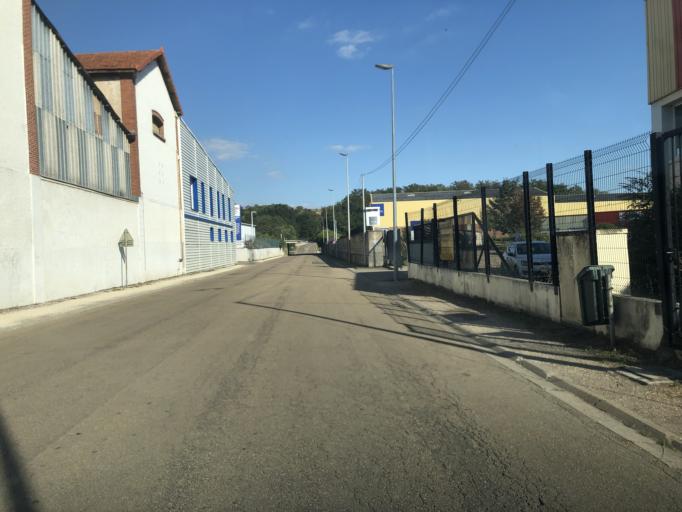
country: FR
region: Bourgogne
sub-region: Departement de l'Yonne
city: Auxerre
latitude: 47.8064
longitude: 3.5845
